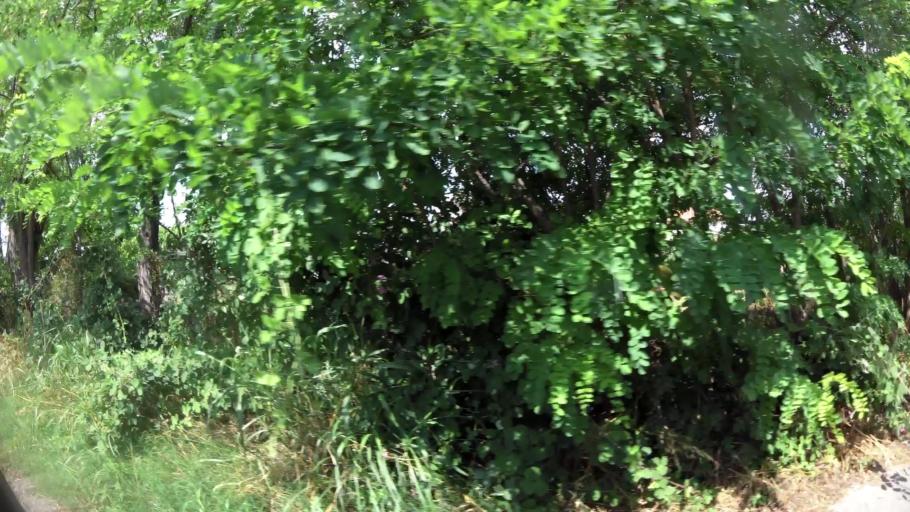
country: GR
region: Central Macedonia
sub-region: Nomos Pierias
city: Makrygialos
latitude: 40.4121
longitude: 22.6045
